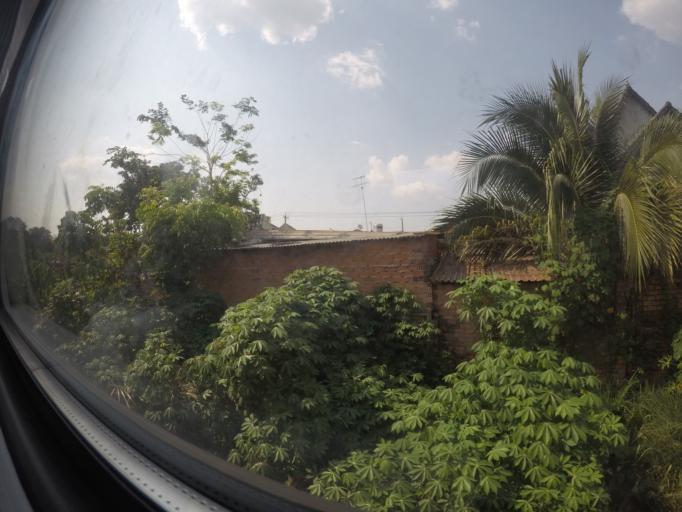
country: VN
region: Dong Nai
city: Long Khanh
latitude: 10.9326
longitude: 107.2351
